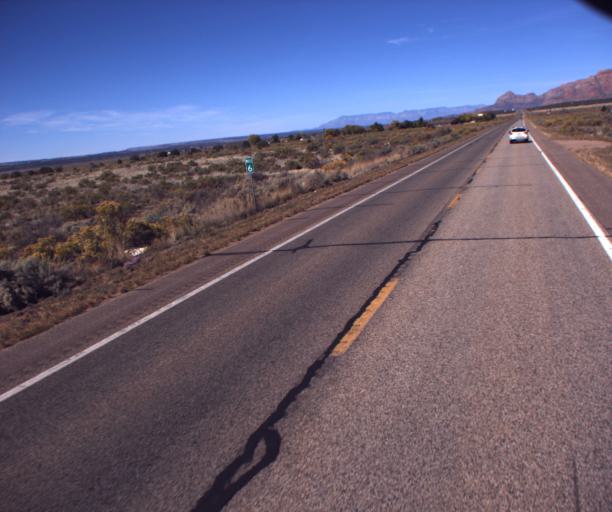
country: US
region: Arizona
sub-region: Mohave County
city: Colorado City
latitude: 36.9263
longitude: -112.9400
